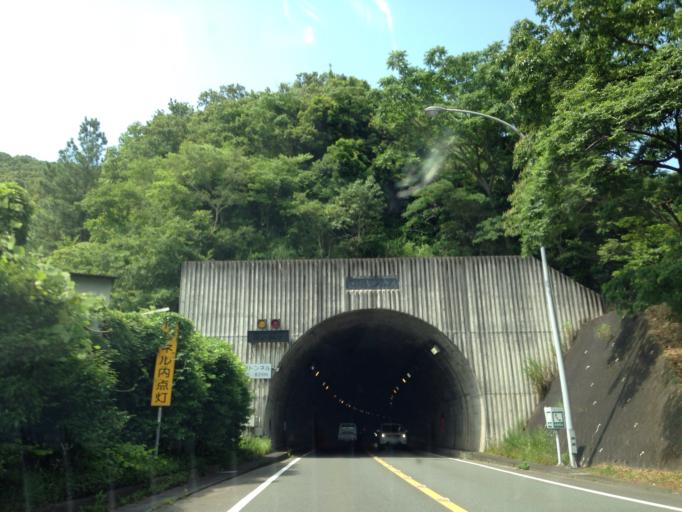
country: JP
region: Shizuoka
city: Mishima
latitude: 35.0599
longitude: 138.9229
